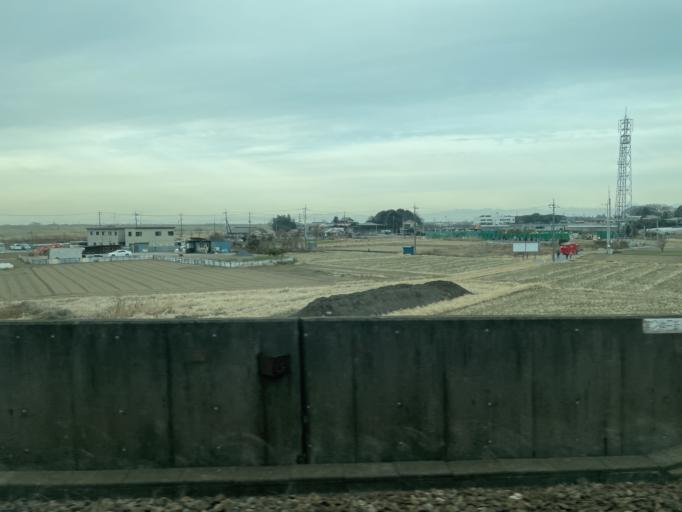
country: JP
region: Saitama
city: Kurihashi
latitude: 36.1528
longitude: 139.7094
